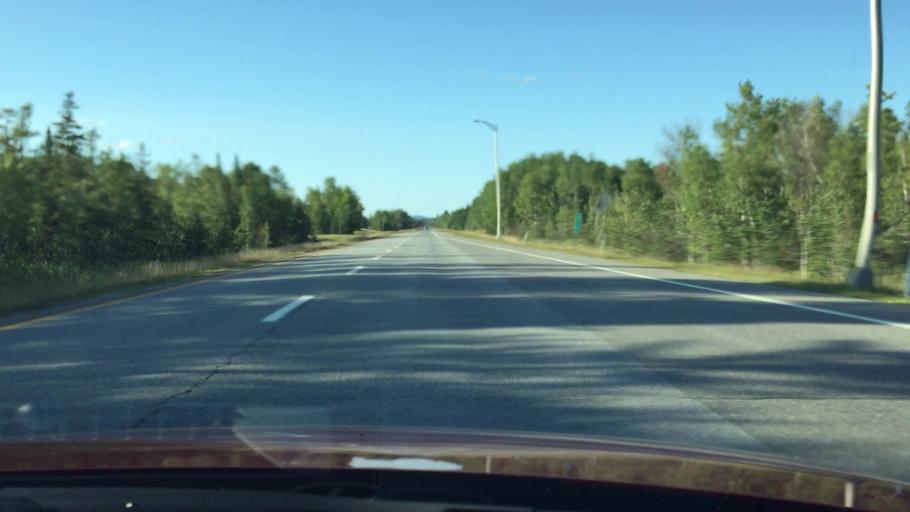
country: US
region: Maine
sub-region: Penobscot County
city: Howland
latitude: 45.2413
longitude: -68.6775
